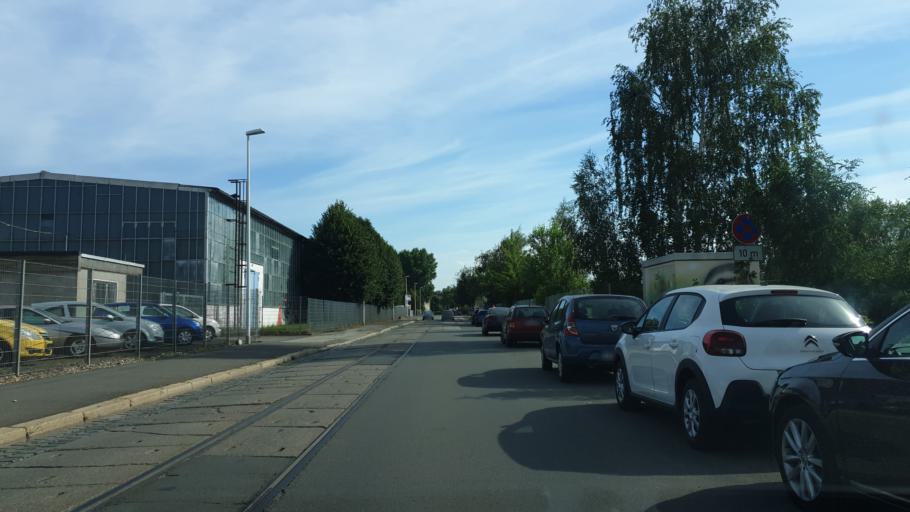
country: DE
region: Thuringia
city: Gera
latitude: 50.8576
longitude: 12.0816
